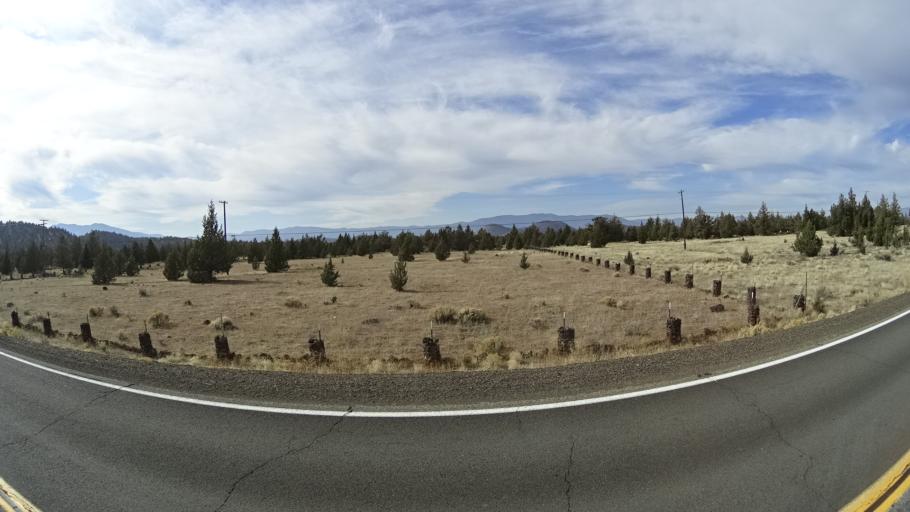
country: US
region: California
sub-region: Siskiyou County
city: Weed
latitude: 41.5853
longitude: -122.3998
